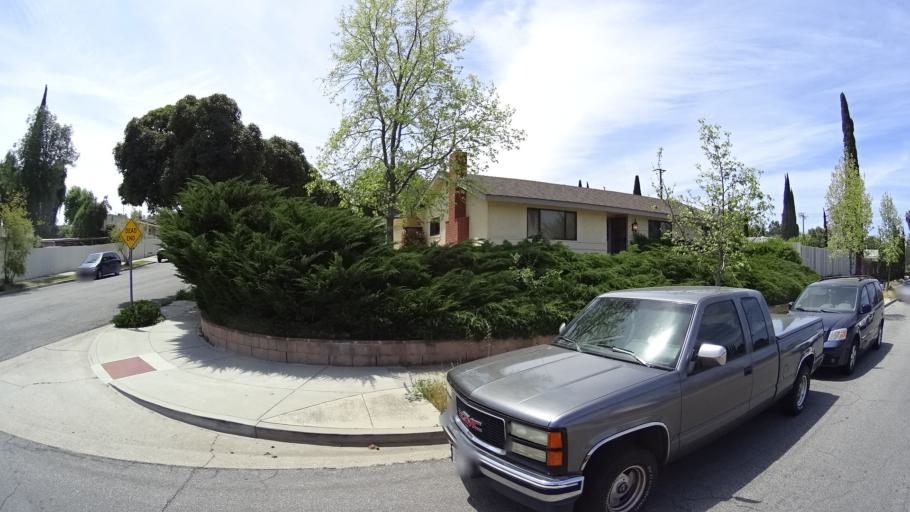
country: US
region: California
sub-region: Ventura County
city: Thousand Oaks
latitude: 34.1978
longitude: -118.8614
